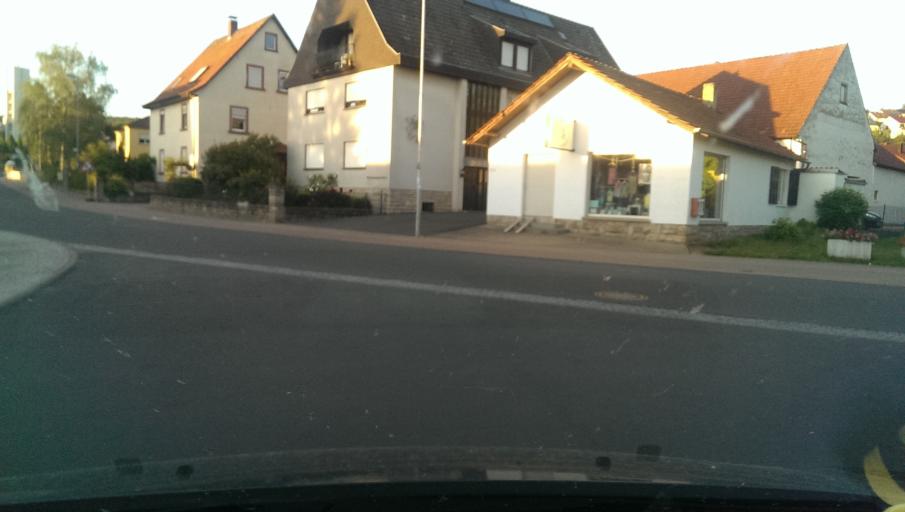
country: DE
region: Baden-Wuerttemberg
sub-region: Regierungsbezirk Stuttgart
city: Tauberbischofsheim
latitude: 49.6250
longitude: 9.6700
